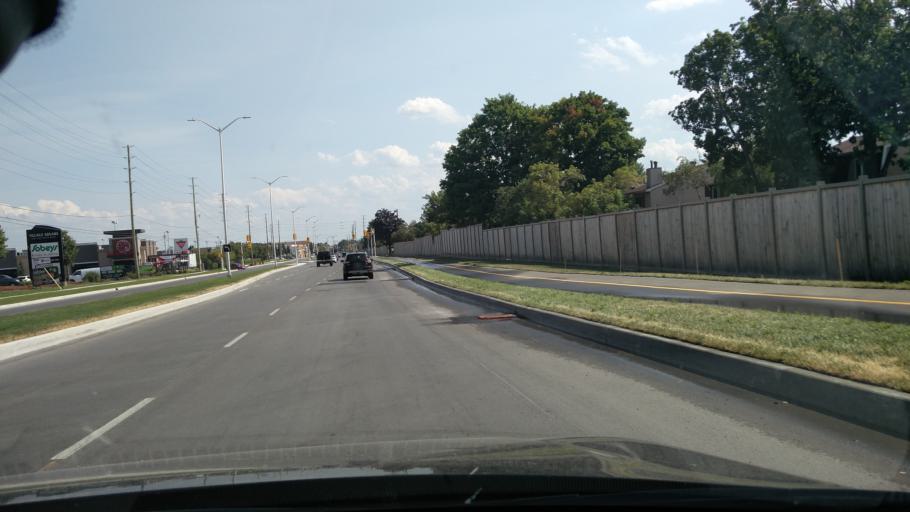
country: CA
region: Ontario
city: Bells Corners
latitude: 45.2741
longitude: -75.7486
